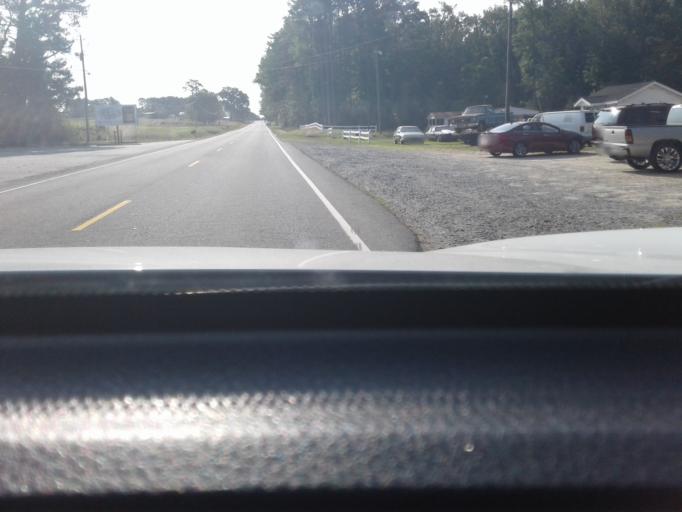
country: US
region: North Carolina
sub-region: Johnston County
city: Benson
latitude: 35.3888
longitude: -78.5731
